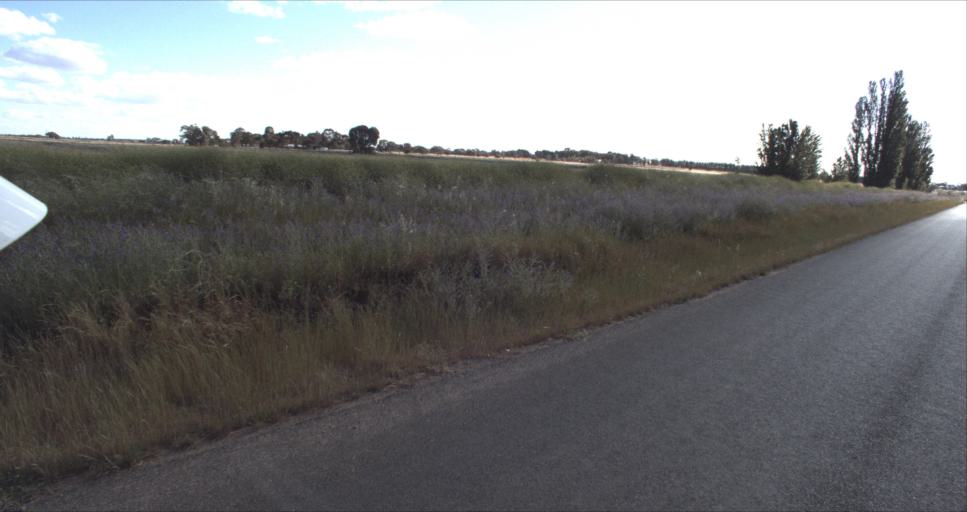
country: AU
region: New South Wales
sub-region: Griffith
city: Griffith
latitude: -34.4385
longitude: 146.2096
